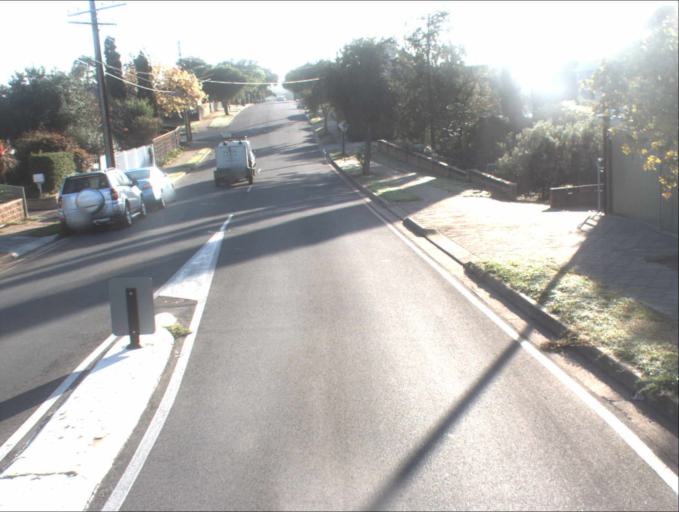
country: AU
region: South Australia
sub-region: Campbelltown
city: Paradise
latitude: -34.8690
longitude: 138.6528
